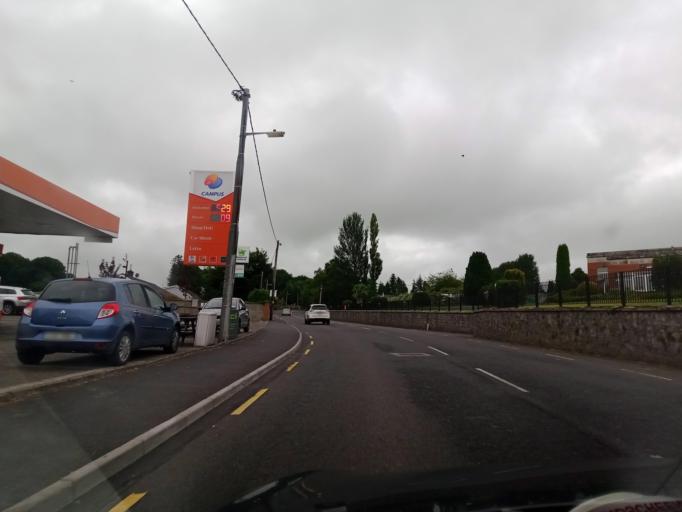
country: IE
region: Leinster
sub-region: Laois
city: Abbeyleix
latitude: 52.9124
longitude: -7.3432
